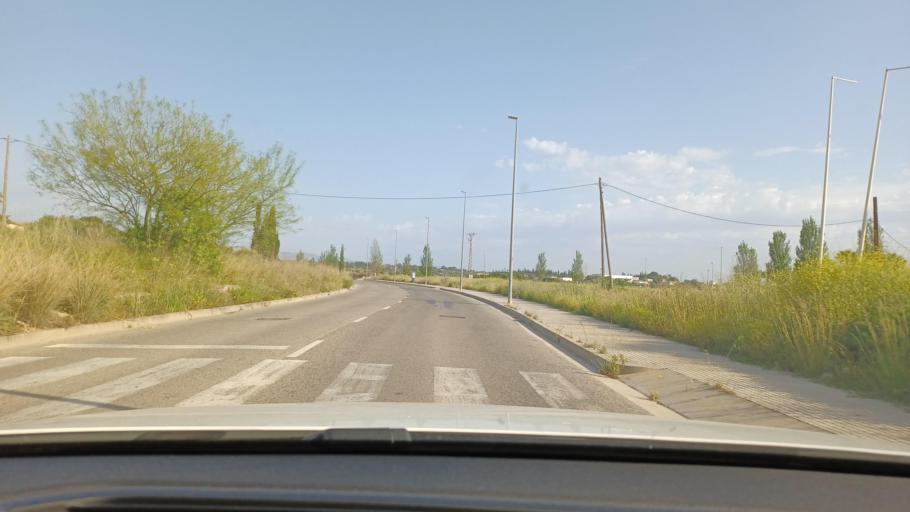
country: ES
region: Catalonia
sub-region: Provincia de Tarragona
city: Amposta
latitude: 40.7092
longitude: 0.5682
